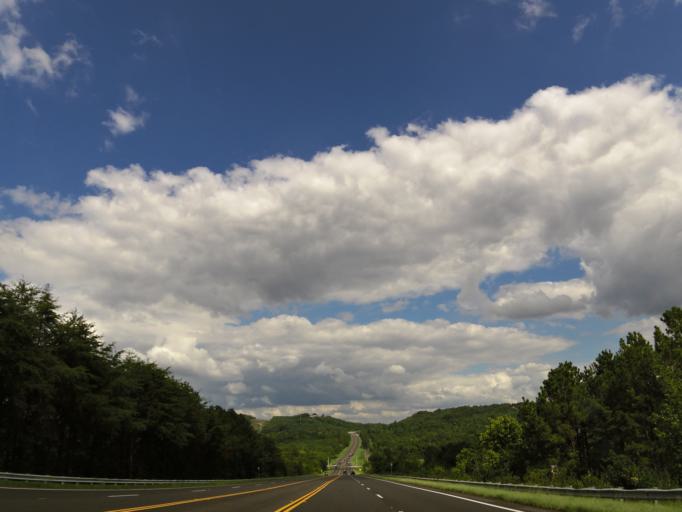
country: US
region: Georgia
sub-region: Walker County
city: Fairview
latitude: 34.9508
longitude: -85.3189
